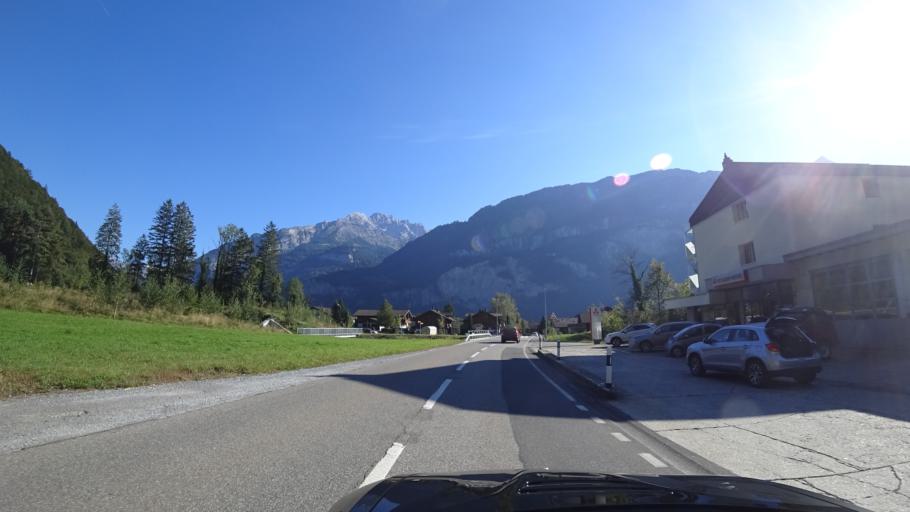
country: CH
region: Bern
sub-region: Interlaken-Oberhasli District
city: Meiringen
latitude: 46.7389
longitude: 8.1680
